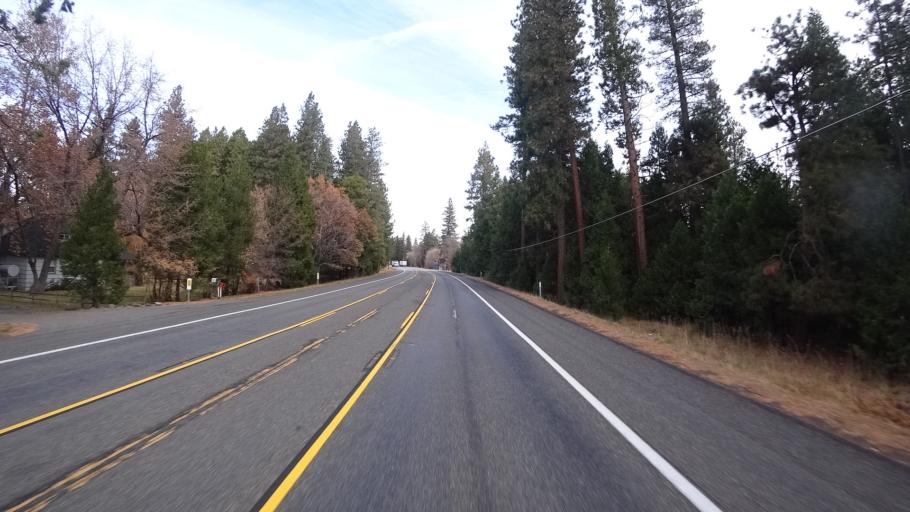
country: US
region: California
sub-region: Siskiyou County
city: Weed
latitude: 41.4469
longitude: -122.3660
